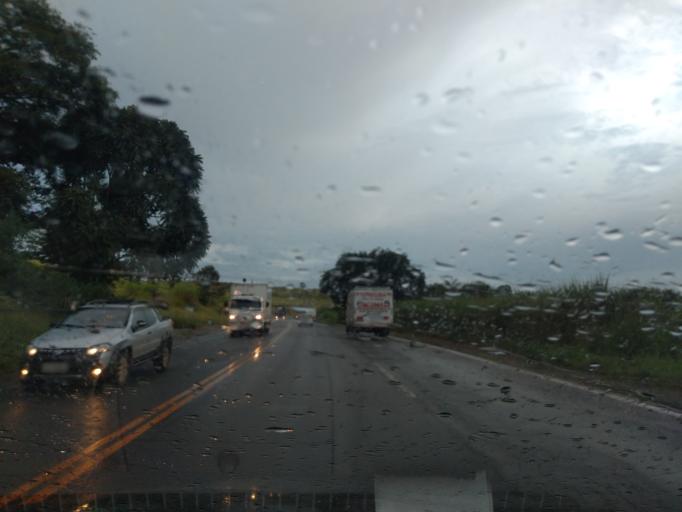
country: BR
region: Minas Gerais
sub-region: Varginha
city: Varginha
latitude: -21.6191
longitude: -45.4183
